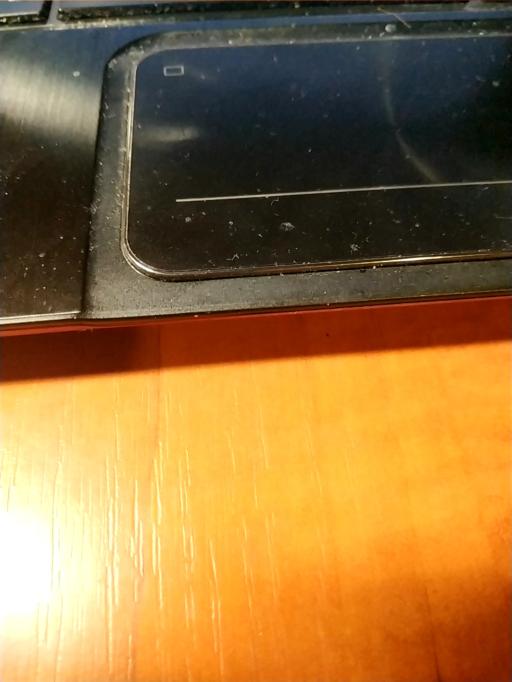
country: RU
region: Tverskaya
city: Rameshki
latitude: 57.2449
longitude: 35.8969
